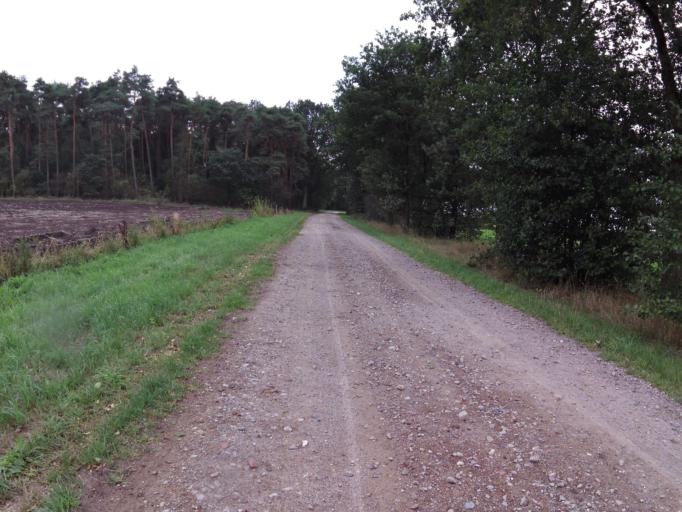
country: DE
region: Lower Saxony
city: Scheessel
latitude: 53.1484
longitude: 9.4488
